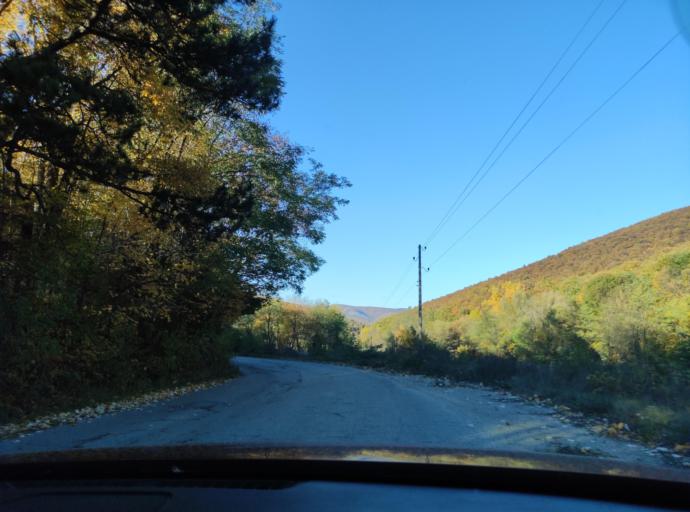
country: BG
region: Montana
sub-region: Obshtina Chiprovtsi
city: Chiprovtsi
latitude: 43.4043
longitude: 22.9381
